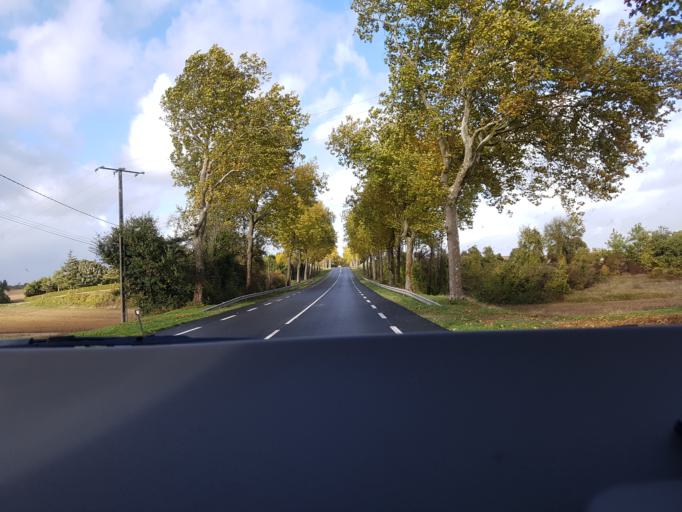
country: FR
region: Poitou-Charentes
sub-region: Departement de la Charente-Maritime
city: Saint-Genis-de-Saintonge
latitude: 45.5106
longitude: -0.5636
